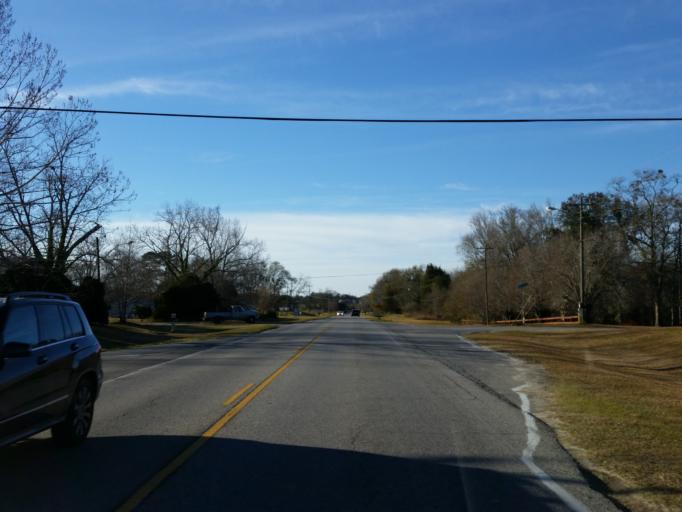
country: US
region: Georgia
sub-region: Lowndes County
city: Remerton
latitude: 30.9041
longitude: -83.3392
